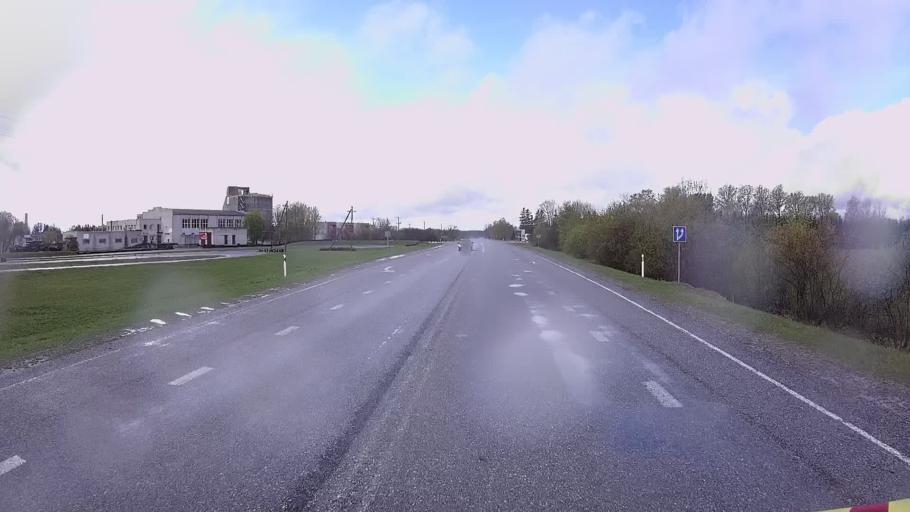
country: EE
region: Hiiumaa
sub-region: Kaerdla linn
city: Kardla
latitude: 58.8324
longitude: 22.7745
